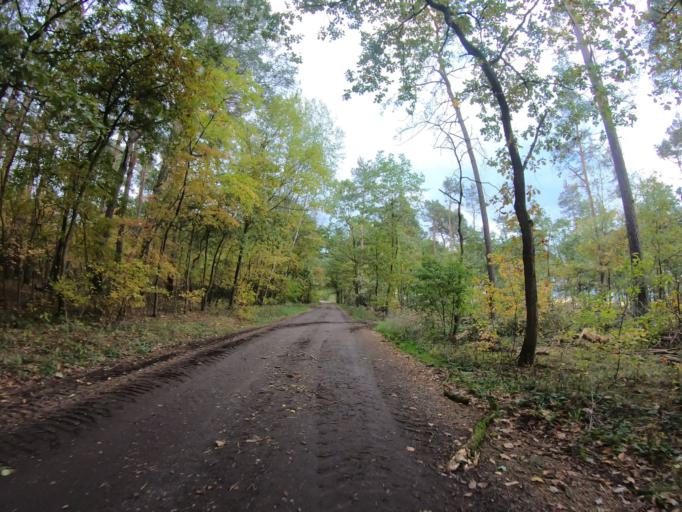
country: DE
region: Lower Saxony
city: Wagenhoff
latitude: 52.5253
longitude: 10.5221
